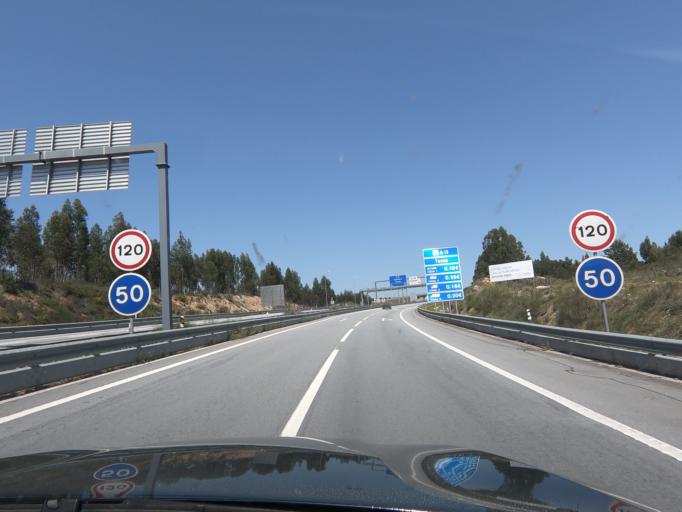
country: PT
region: Santarem
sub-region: Entroncamento
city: Entroncamento
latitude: 39.4914
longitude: -8.4461
